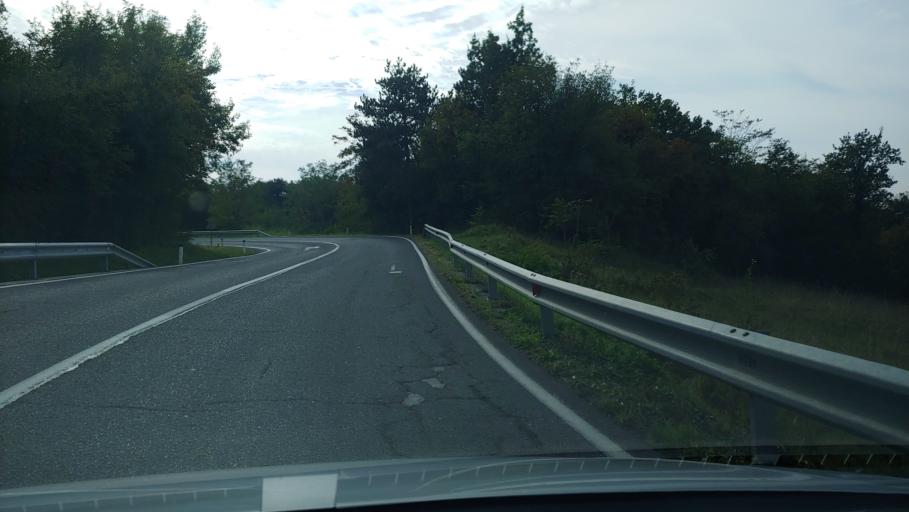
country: SI
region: Nova Gorica
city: Sempas
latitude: 45.9124
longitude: 13.7678
